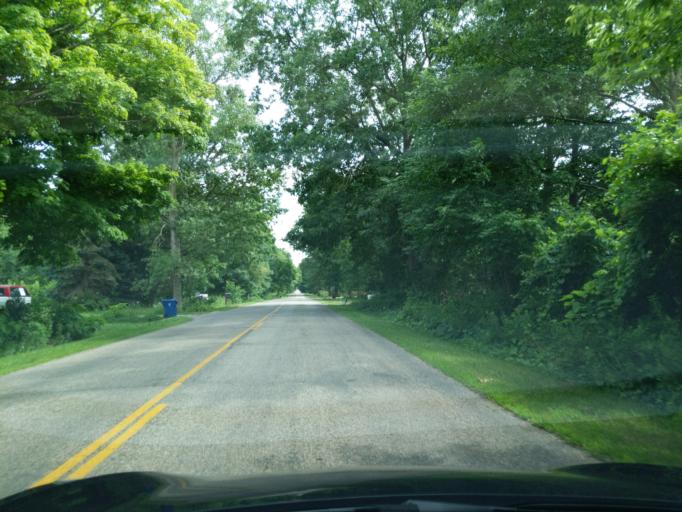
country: US
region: Michigan
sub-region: Eaton County
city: Eaton Rapids
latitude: 42.5672
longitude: -84.6021
